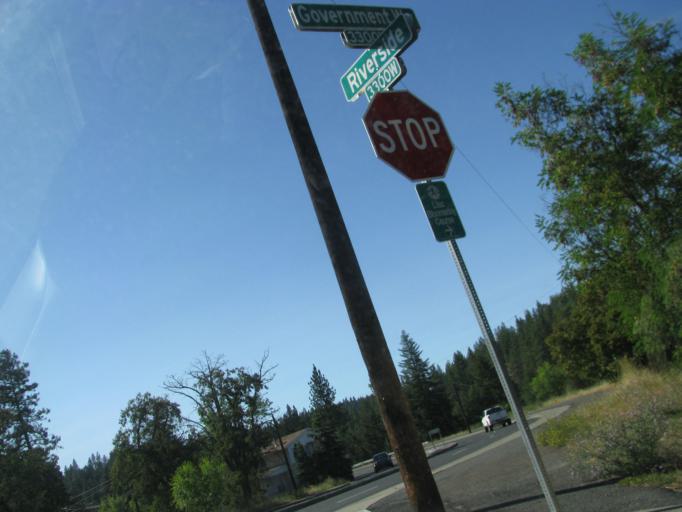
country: US
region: Washington
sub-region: Spokane County
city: Spokane
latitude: 47.6554
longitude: -117.4612
